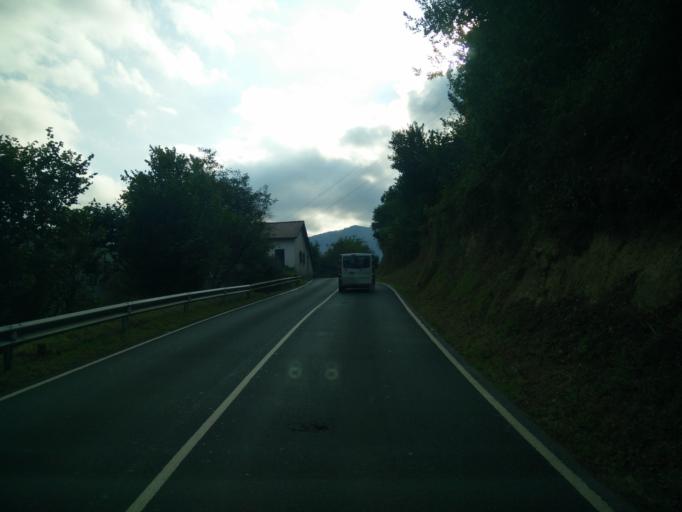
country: ES
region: Basque Country
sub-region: Bizkaia
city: Berriatua
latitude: 43.2937
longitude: -2.4781
